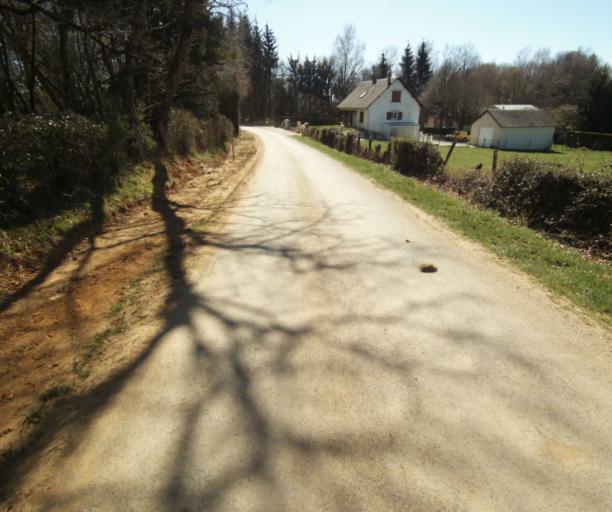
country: FR
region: Limousin
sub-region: Departement de la Correze
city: Saint-Clement
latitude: 45.3763
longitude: 1.6788
